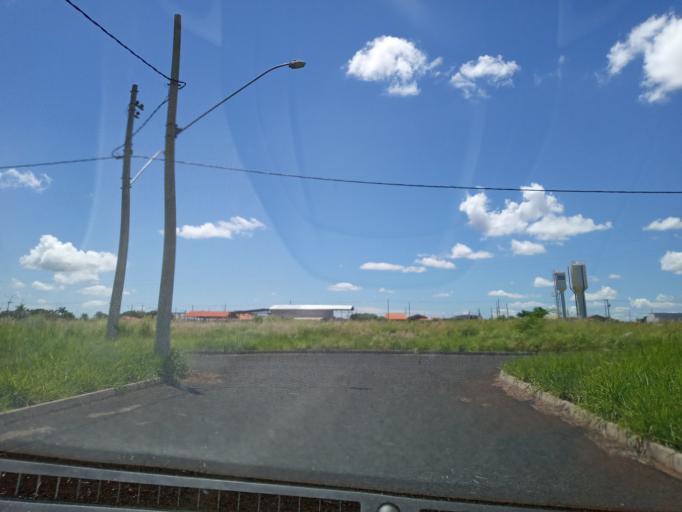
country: BR
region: Minas Gerais
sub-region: Centralina
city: Centralina
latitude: -18.5992
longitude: -49.1971
